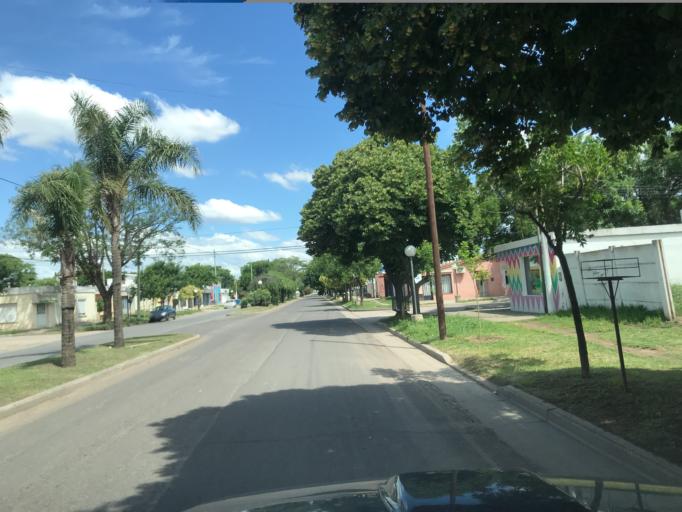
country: AR
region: Cordoba
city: Las Perdices
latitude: -32.7535
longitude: -63.7844
